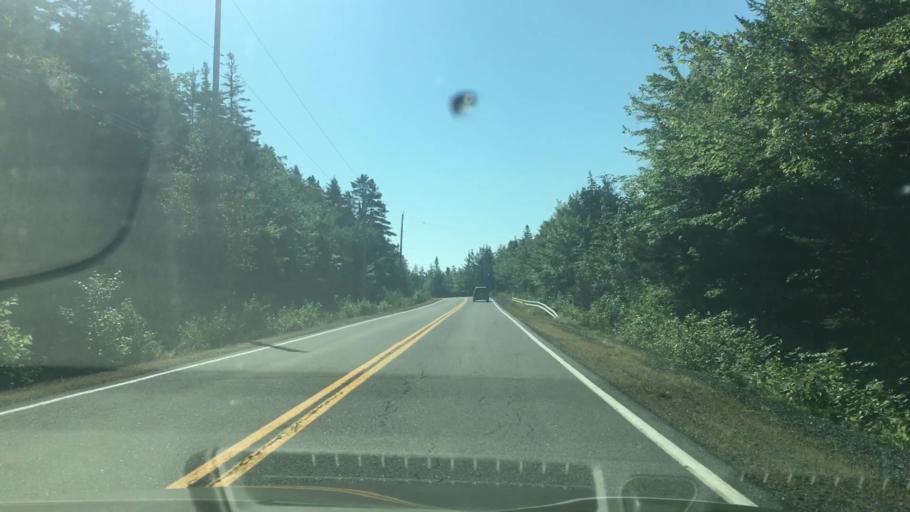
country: CA
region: Nova Scotia
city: Cole Harbour
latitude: 44.8097
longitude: -62.8351
